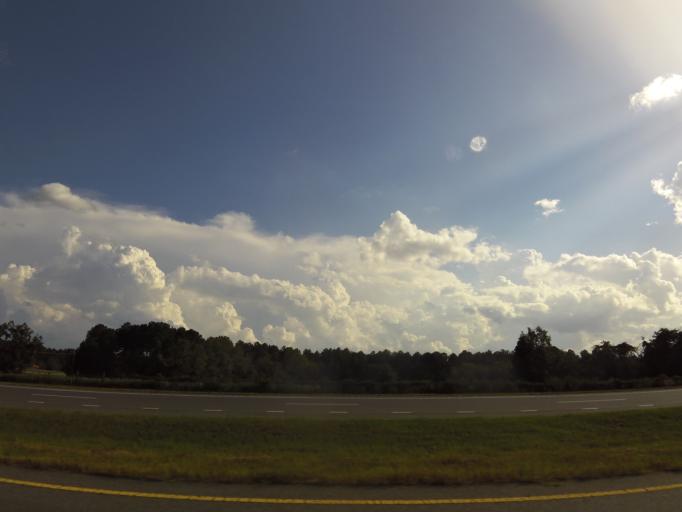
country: US
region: Georgia
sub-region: Brooks County
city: Quitman
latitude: 30.7850
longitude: -83.6241
